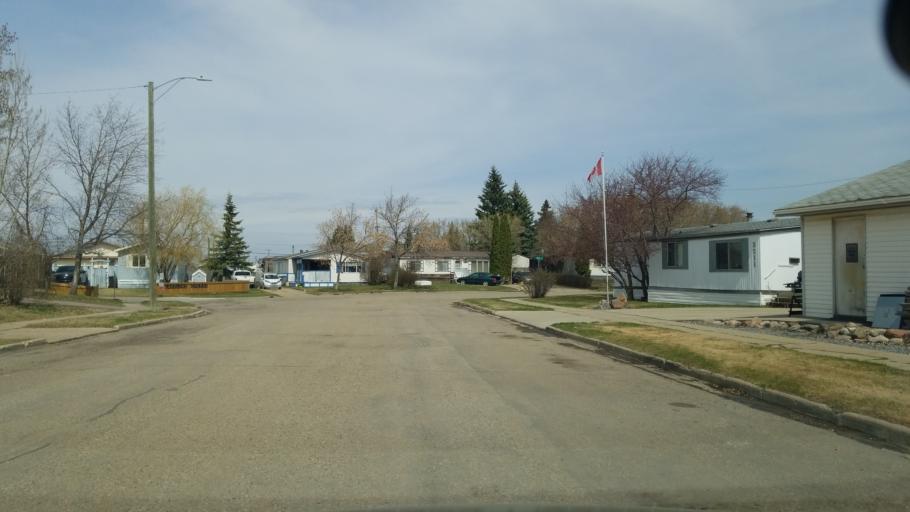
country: CA
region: Saskatchewan
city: Lloydminster
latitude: 53.2916
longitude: -110.0124
